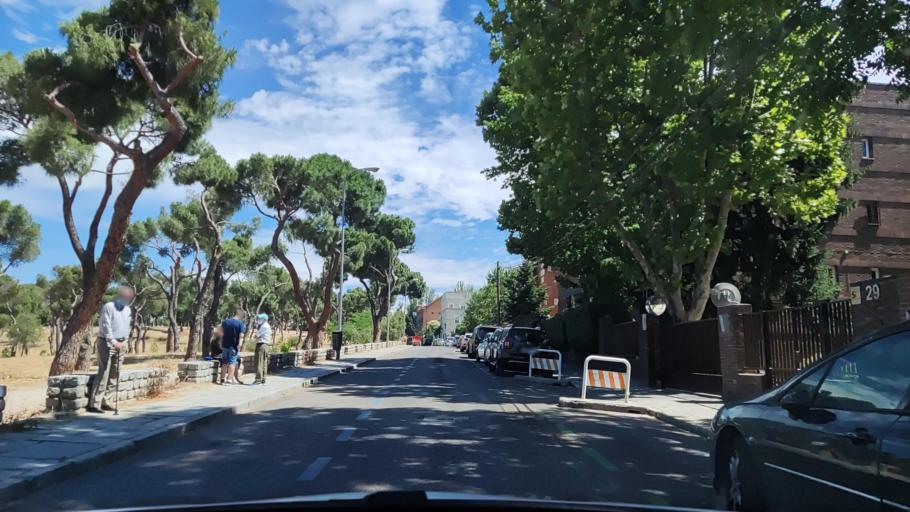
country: ES
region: Madrid
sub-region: Provincia de Madrid
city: Tetuan de las Victorias
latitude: 40.4553
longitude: -3.7175
